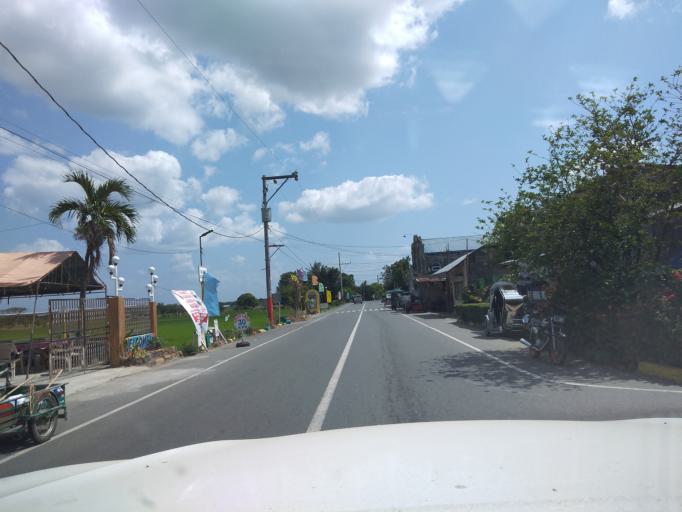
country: PH
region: Central Luzon
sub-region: Province of Pampanga
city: Bahay Pare
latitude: 15.0466
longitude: 120.8780
